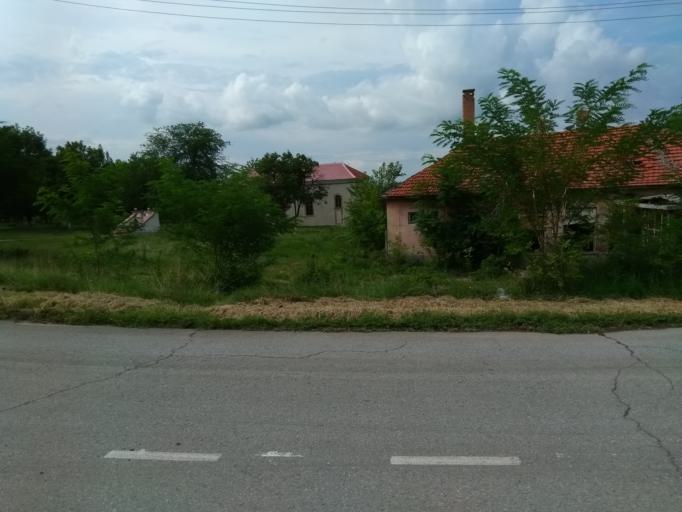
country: BG
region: Sliven
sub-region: Obshtina Sliven
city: Kermen
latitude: 42.4578
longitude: 26.1445
